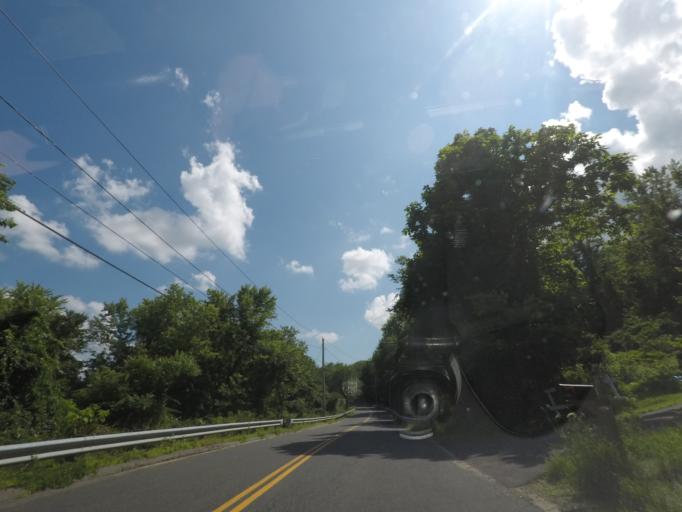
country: US
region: Massachusetts
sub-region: Hampden County
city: Palmer
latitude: 42.1363
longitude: -72.3335
